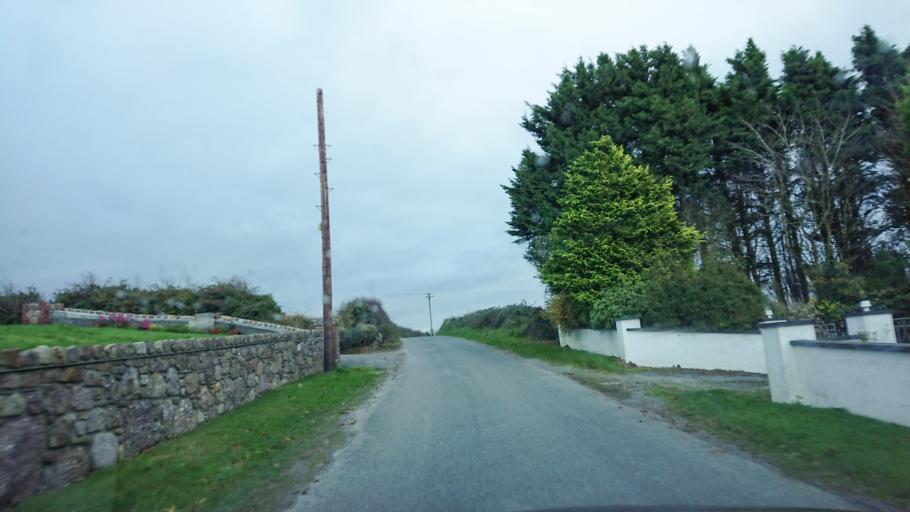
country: IE
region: Munster
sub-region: Waterford
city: Dunmore East
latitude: 52.2477
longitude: -7.0033
